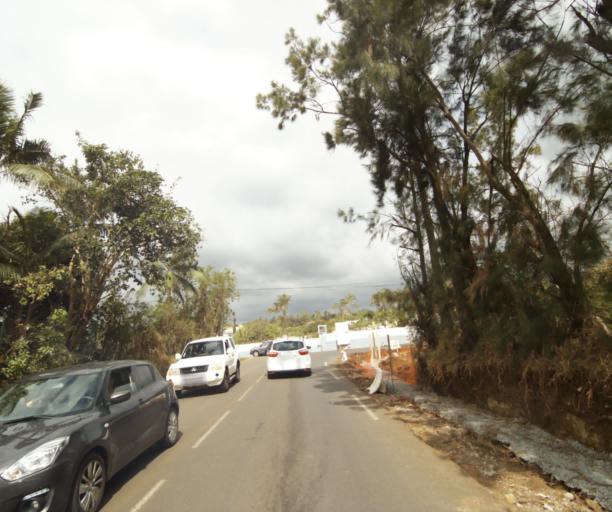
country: RE
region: Reunion
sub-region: Reunion
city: Saint-Paul
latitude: -21.0370
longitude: 55.2885
